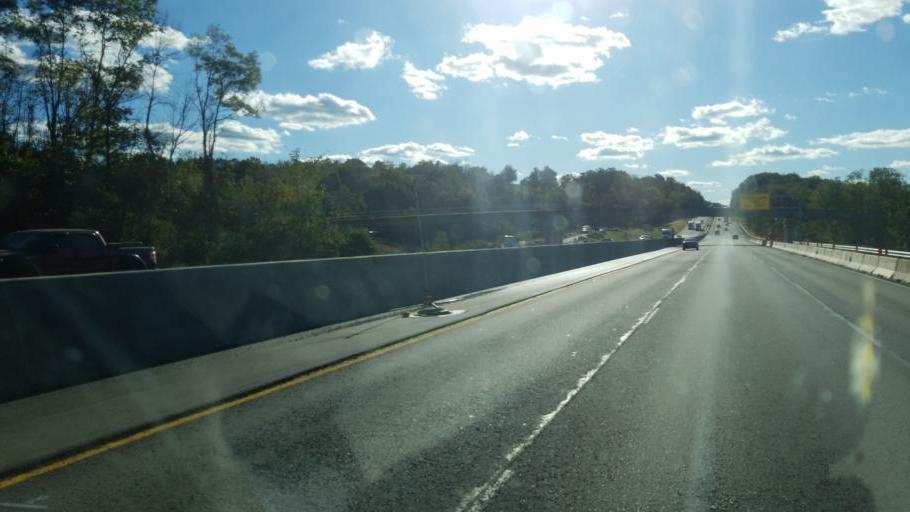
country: US
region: Ohio
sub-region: Belmont County
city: Saint Clairsville
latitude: 40.0708
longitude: -80.8783
